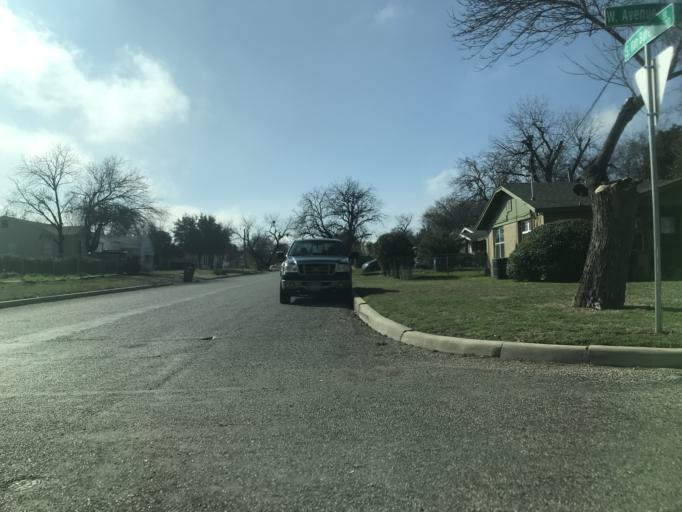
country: US
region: Texas
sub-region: Tom Green County
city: San Angelo
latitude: 31.4486
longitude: -100.4573
